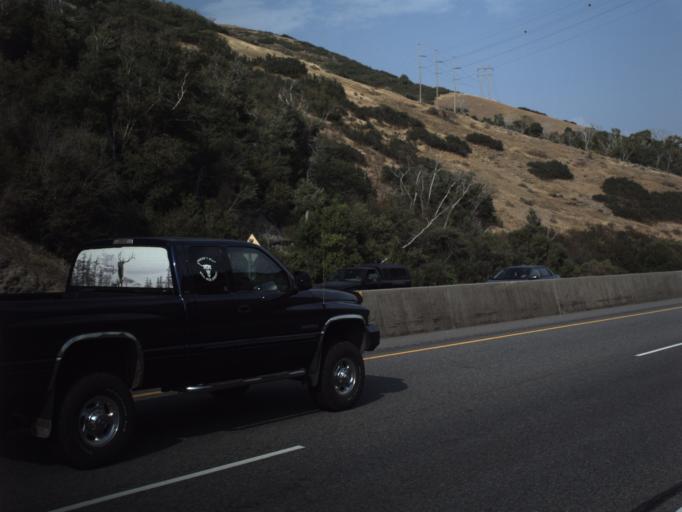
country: US
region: Utah
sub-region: Salt Lake County
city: Mount Olympus
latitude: 40.7421
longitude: -111.7384
